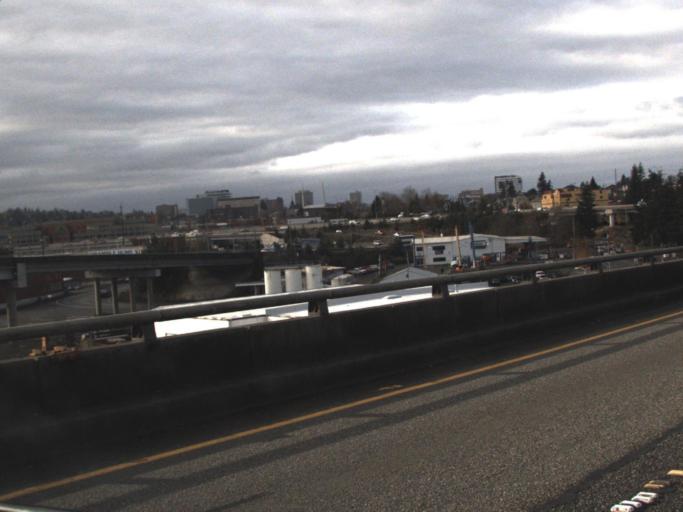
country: US
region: Washington
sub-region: Snohomish County
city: Everett
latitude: 47.9799
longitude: -122.1821
